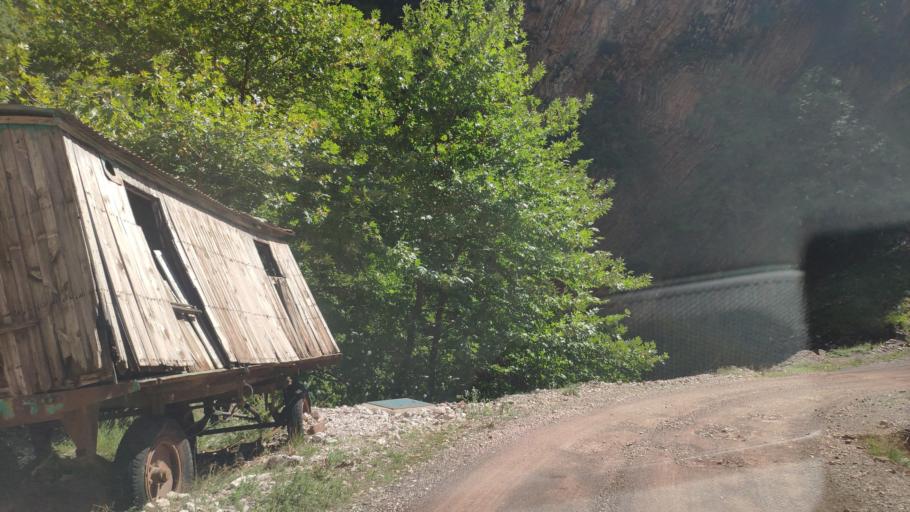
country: GR
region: Central Greece
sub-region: Nomos Evrytanias
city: Kerasochori
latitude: 39.1423
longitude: 21.6584
